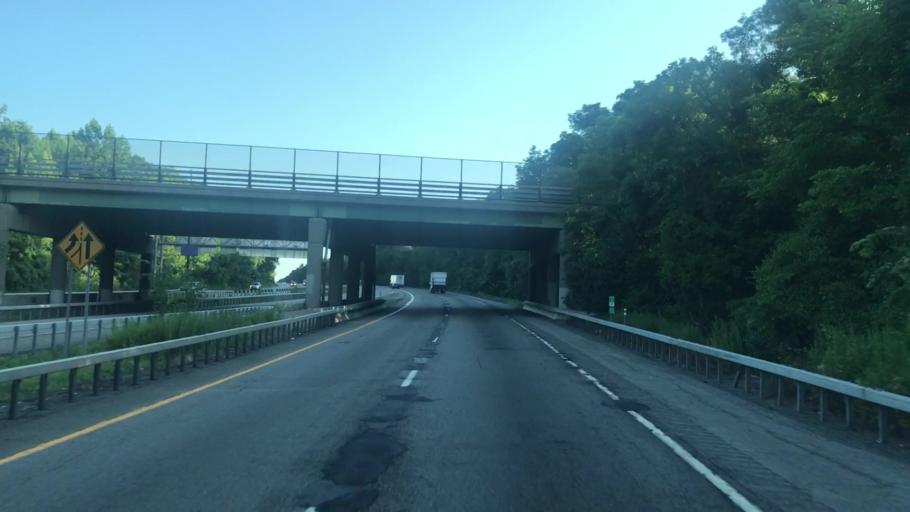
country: US
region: New York
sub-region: Westchester County
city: Purchase
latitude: 41.0337
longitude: -73.7225
